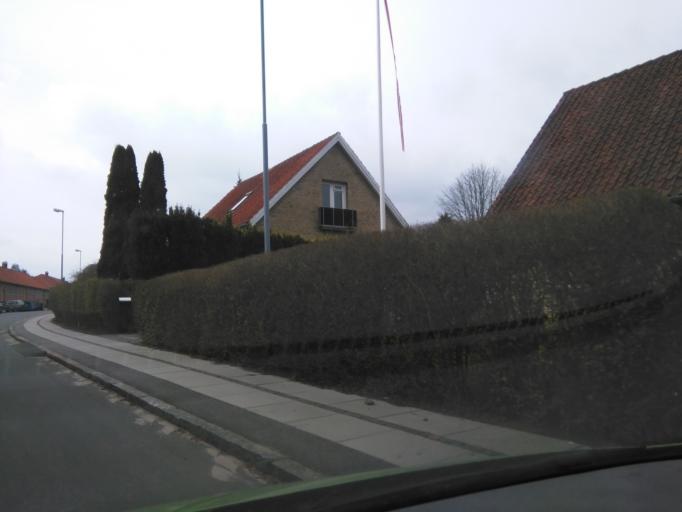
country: DK
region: Central Jutland
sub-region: Arhus Kommune
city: Arhus
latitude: 56.1187
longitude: 10.2024
